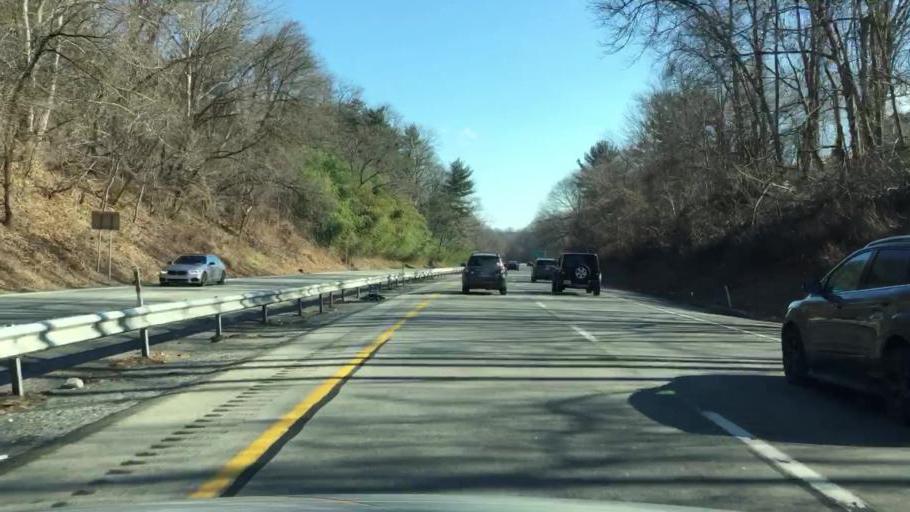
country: US
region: Pennsylvania
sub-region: Delaware County
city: Media
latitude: 39.9366
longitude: -75.3851
